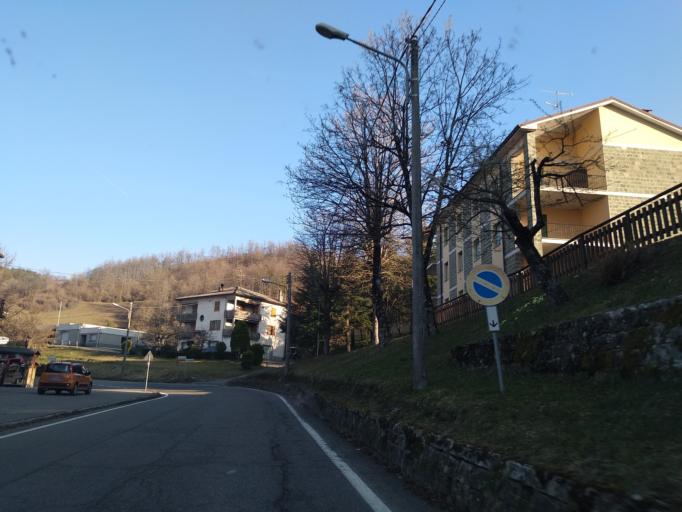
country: IT
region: Emilia-Romagna
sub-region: Provincia di Reggio Emilia
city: Ramiseto
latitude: 44.4115
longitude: 10.2797
